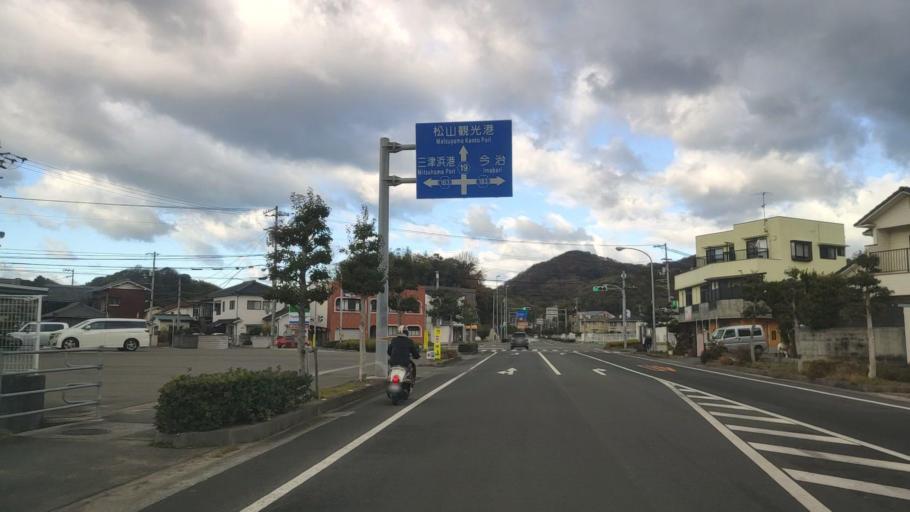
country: JP
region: Ehime
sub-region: Shikoku-chuo Shi
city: Matsuyama
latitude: 33.8714
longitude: 132.7204
